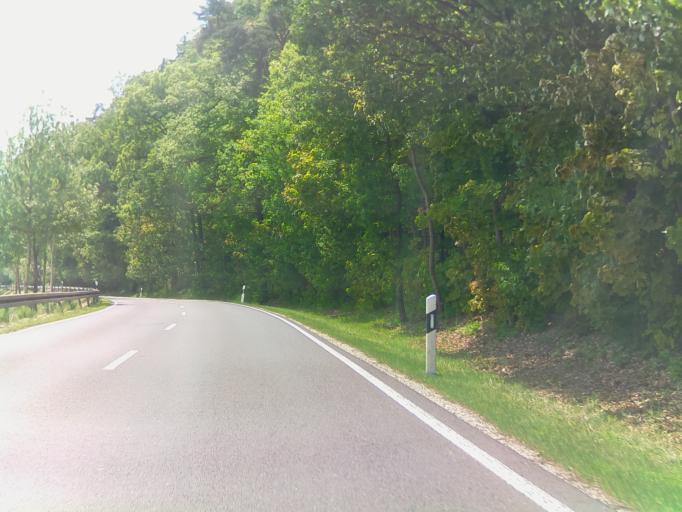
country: DE
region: Thuringia
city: Rudolstadt
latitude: 50.7676
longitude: 11.3109
